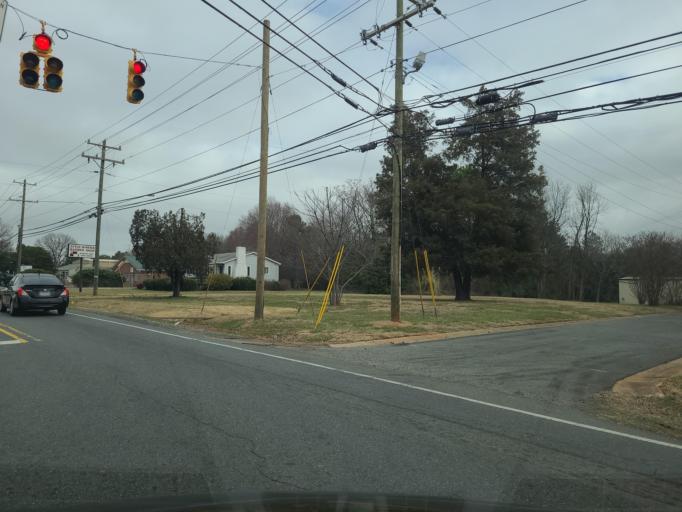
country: US
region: North Carolina
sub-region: Mecklenburg County
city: Mint Hill
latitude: 35.2054
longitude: -80.6703
